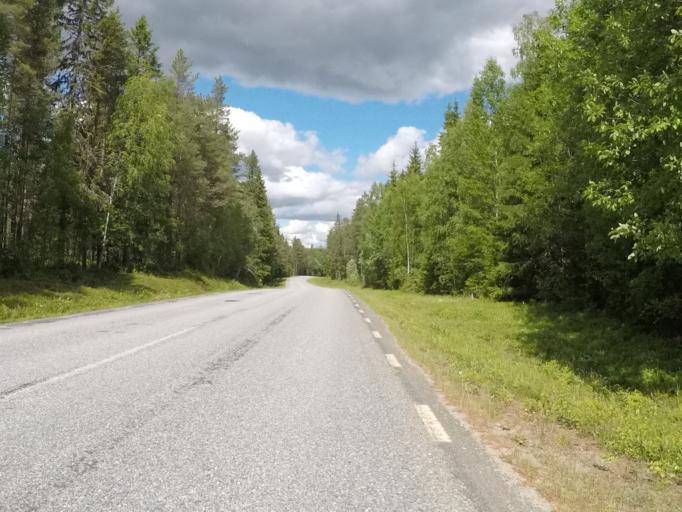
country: SE
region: Vaesterbotten
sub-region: Robertsfors Kommun
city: Robertsfors
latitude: 63.9742
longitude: 20.8101
